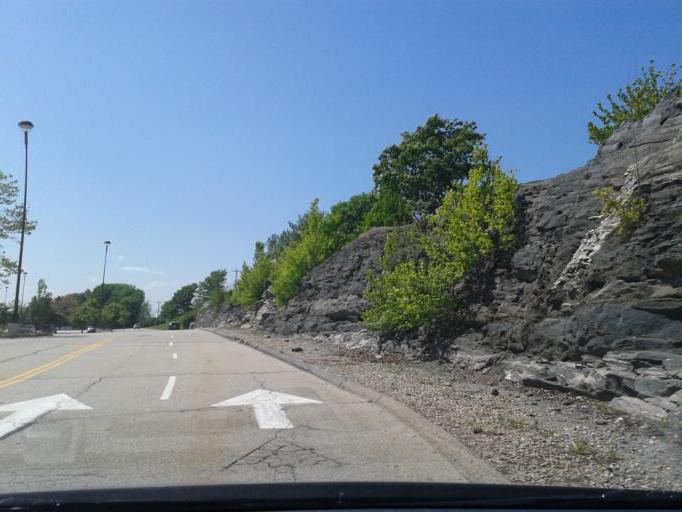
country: US
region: Connecticut
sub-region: New London County
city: Central Waterford
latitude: 41.3754
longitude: -72.1425
